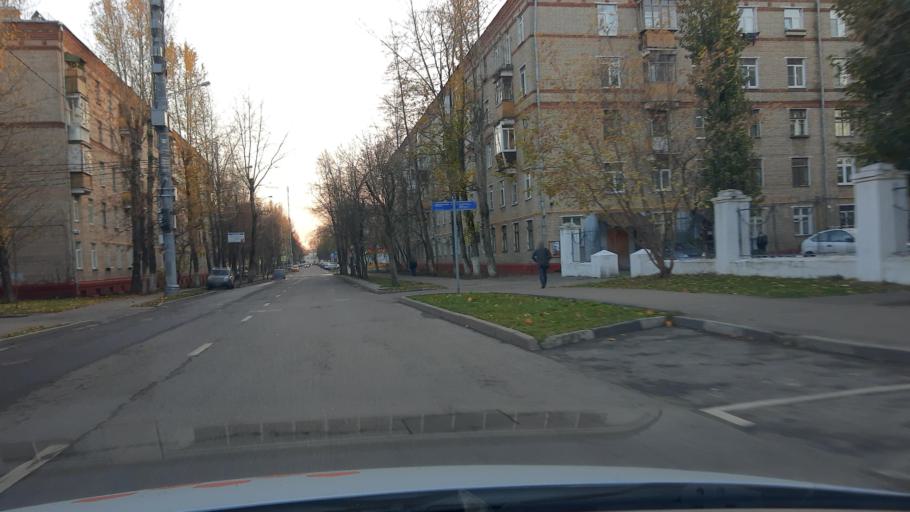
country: RU
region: Moscow
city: Novyye Kuz'minki
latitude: 55.6988
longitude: 37.7473
